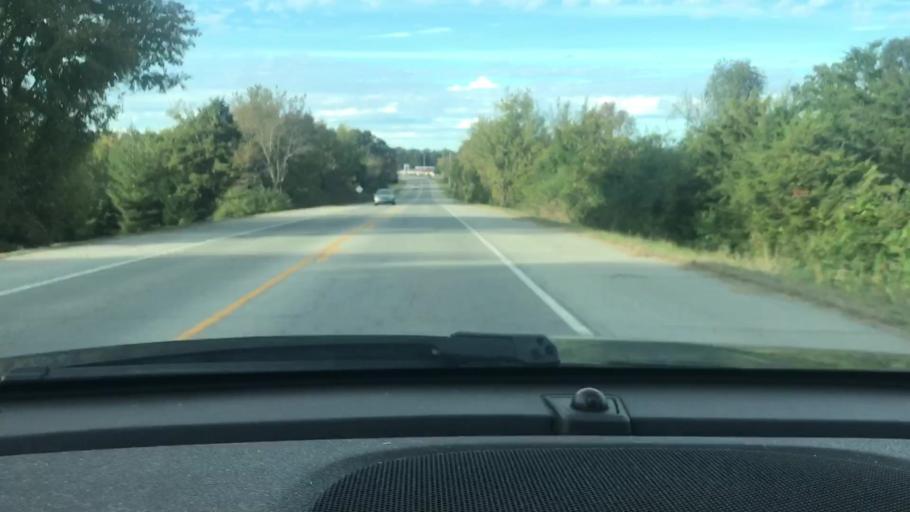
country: US
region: Tennessee
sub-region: Dickson County
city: White Bluff
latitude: 36.1212
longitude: -87.2268
